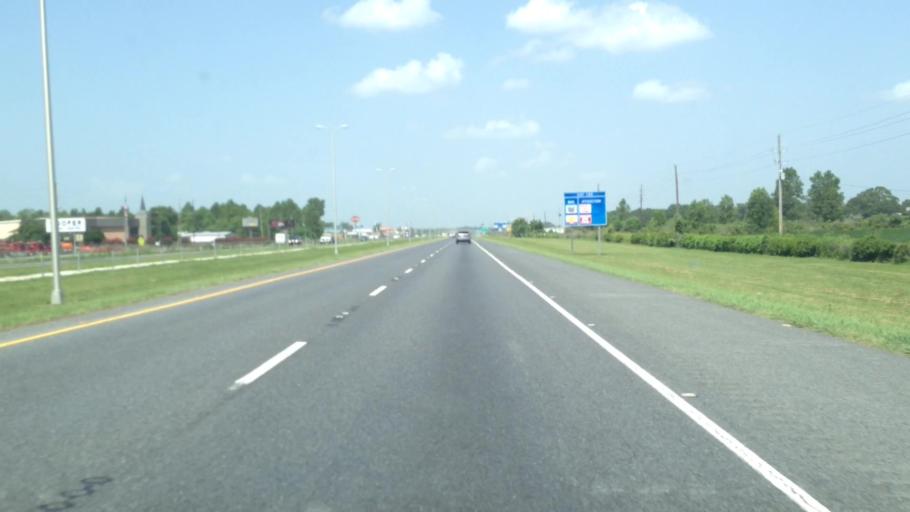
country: US
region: Louisiana
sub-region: Ouachita Parish
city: Lakeshore
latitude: 32.4929
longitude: -92.0349
